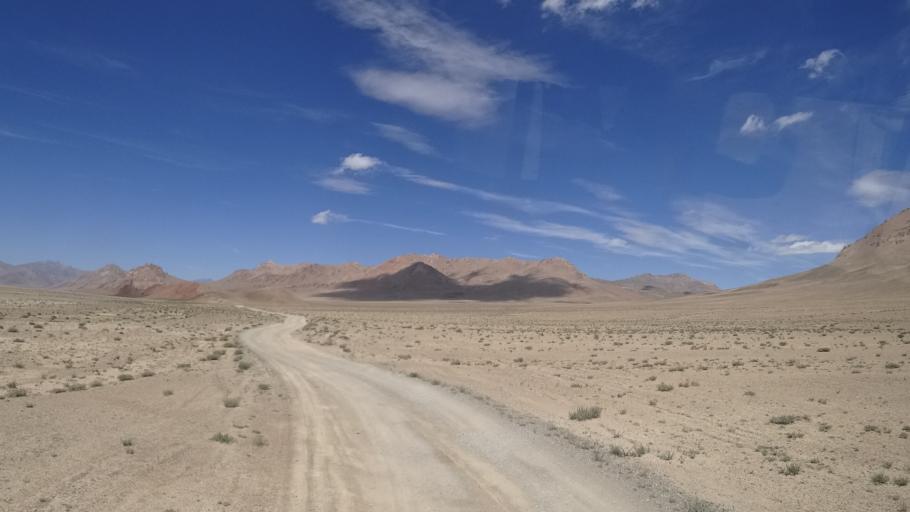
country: TJ
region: Gorno-Badakhshan
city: Murghob
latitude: 37.8822
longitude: 74.1183
